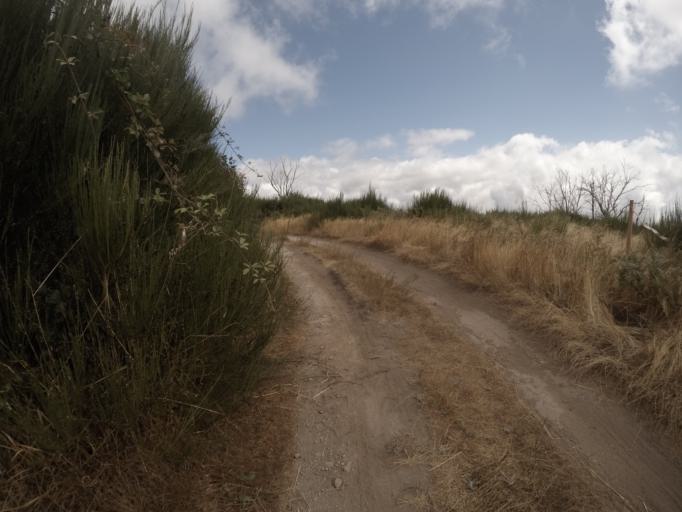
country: PT
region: Madeira
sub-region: Camara de Lobos
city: Curral das Freiras
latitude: 32.7112
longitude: -16.9927
